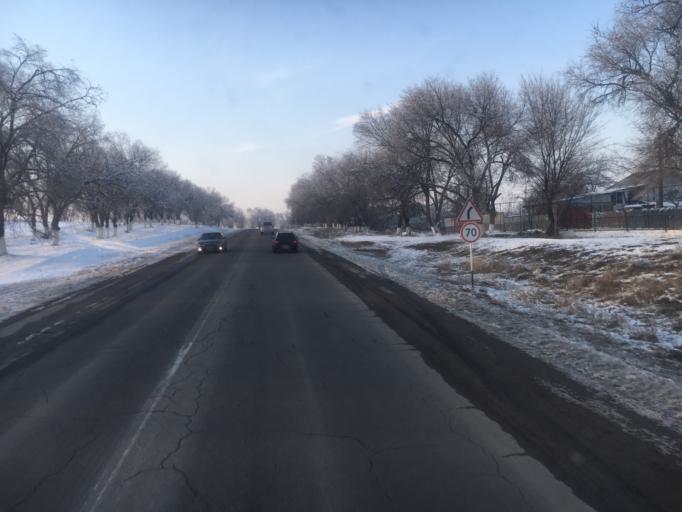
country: KZ
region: Almaty Oblysy
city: Burunday
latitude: 43.3062
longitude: 76.6691
